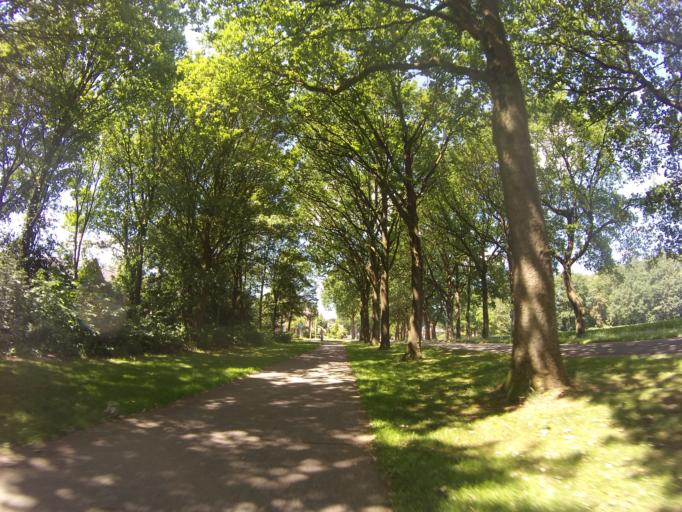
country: NL
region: Drenthe
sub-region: Gemeente Emmen
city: Emmen
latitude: 52.8485
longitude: 6.8568
